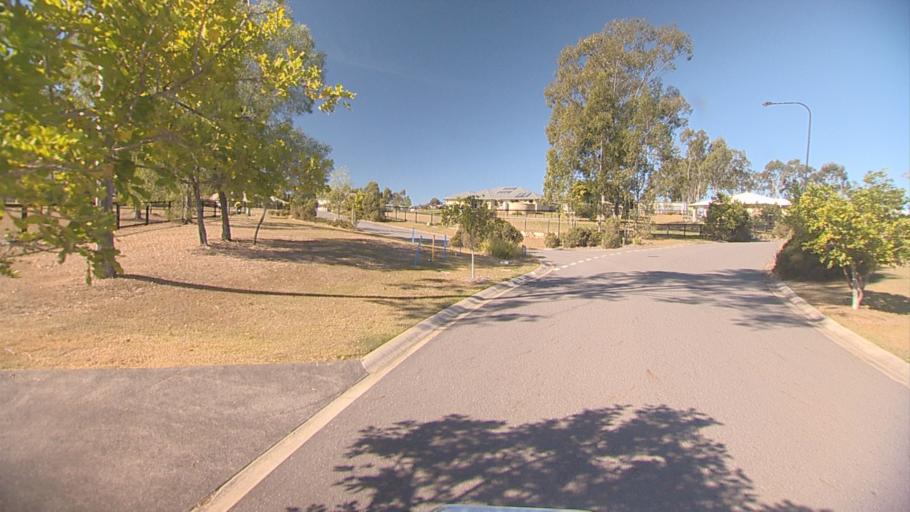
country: AU
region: Queensland
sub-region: Logan
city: North Maclean
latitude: -27.8257
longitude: 152.9812
